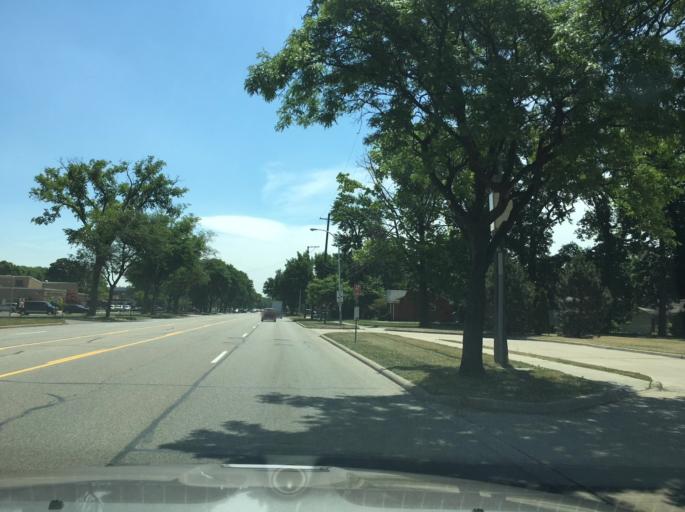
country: US
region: Michigan
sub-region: Wayne County
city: Allen Park
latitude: 42.2944
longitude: -83.2183
